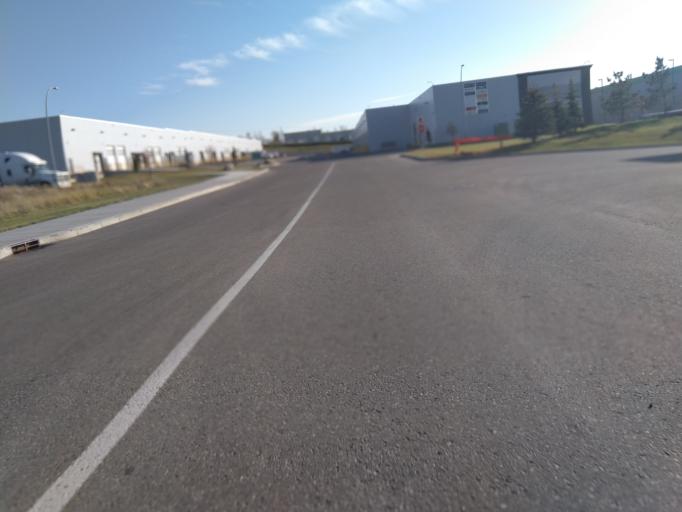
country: CA
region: Alberta
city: Calgary
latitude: 51.1061
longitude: -114.0413
